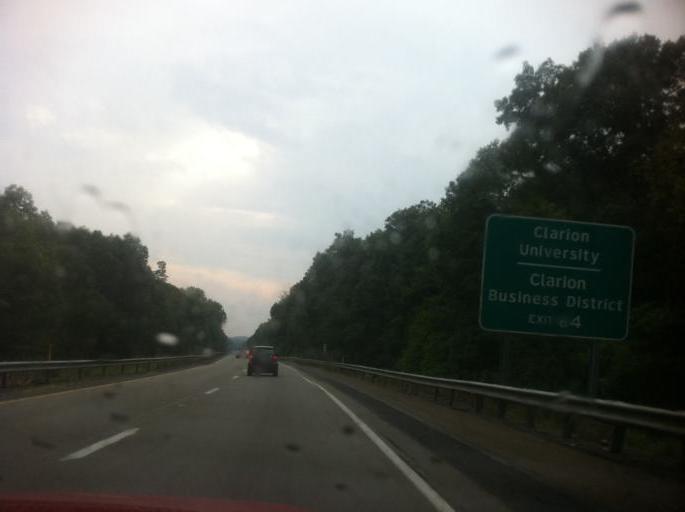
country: US
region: Pennsylvania
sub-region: Clarion County
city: Clarion
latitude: 41.1815
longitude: -79.3171
